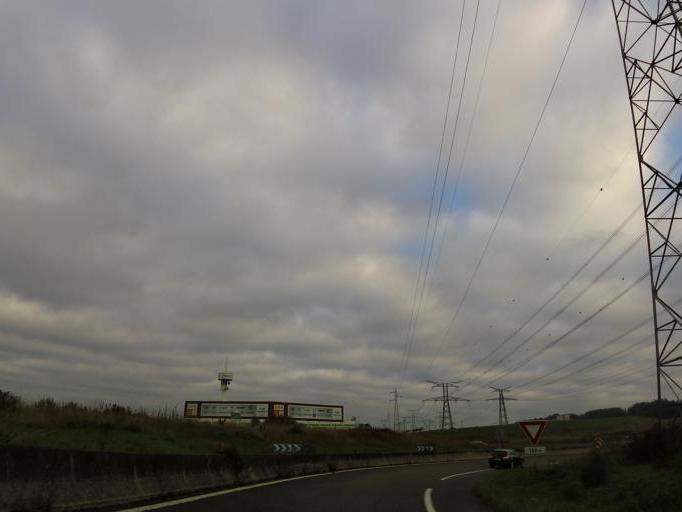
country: FR
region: Ile-de-France
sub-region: Departement de Seine-et-Marne
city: Croissy-Beaubourg
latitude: 48.8313
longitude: 2.6640
